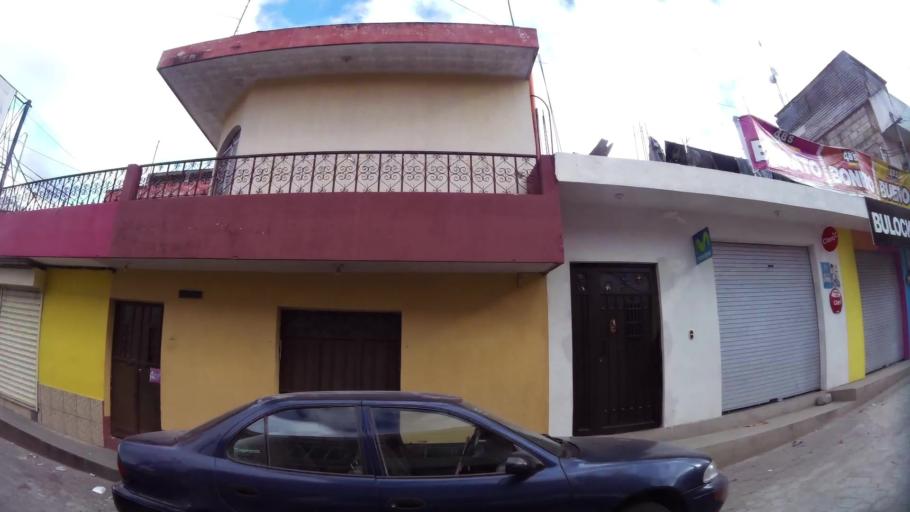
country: GT
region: Quetzaltenango
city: Salcaja
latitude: 14.8795
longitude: -91.4558
